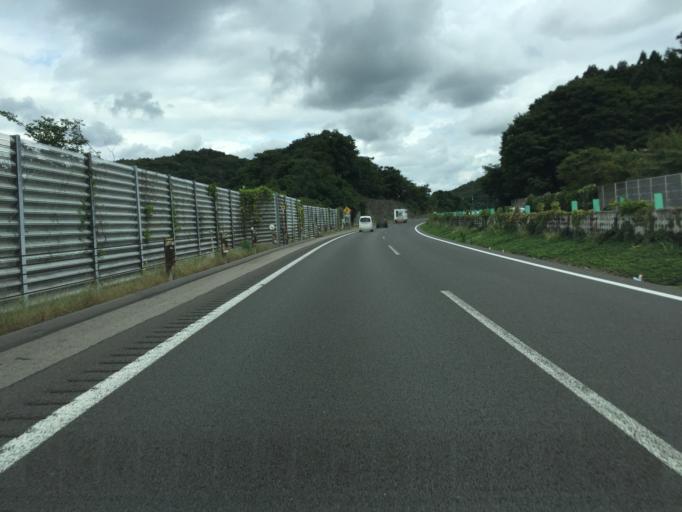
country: JP
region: Miyagi
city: Shiroishi
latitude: 37.9356
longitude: 140.6090
